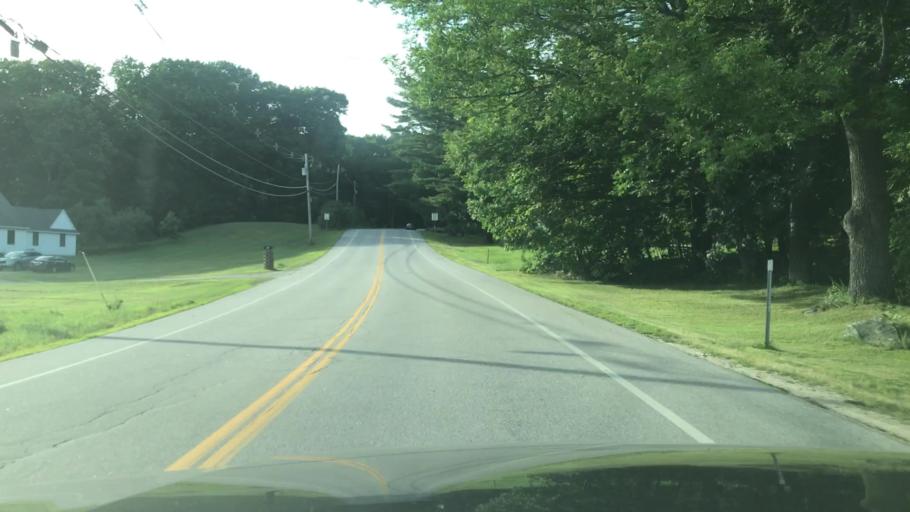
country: US
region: New Hampshire
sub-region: Strafford County
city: Madbury
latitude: 43.1622
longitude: -70.9343
